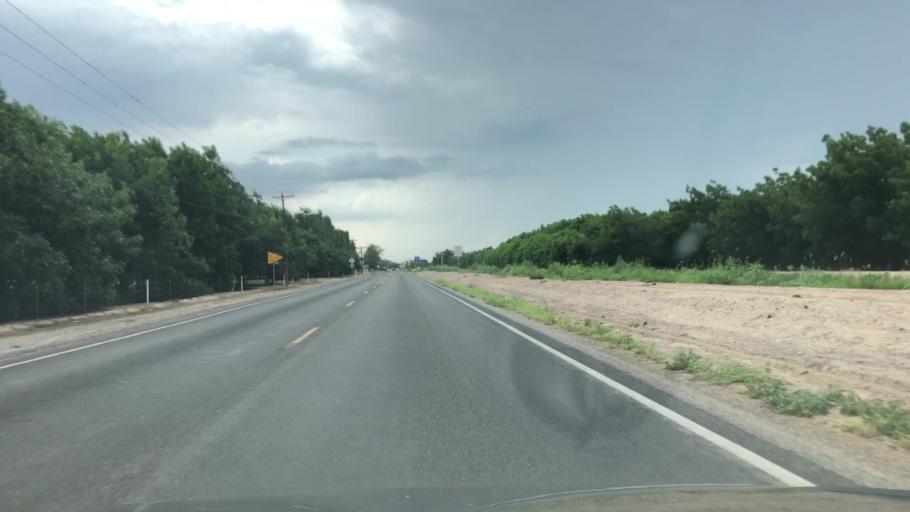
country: US
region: New Mexico
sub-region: Dona Ana County
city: La Union
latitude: 31.9931
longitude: -106.6525
